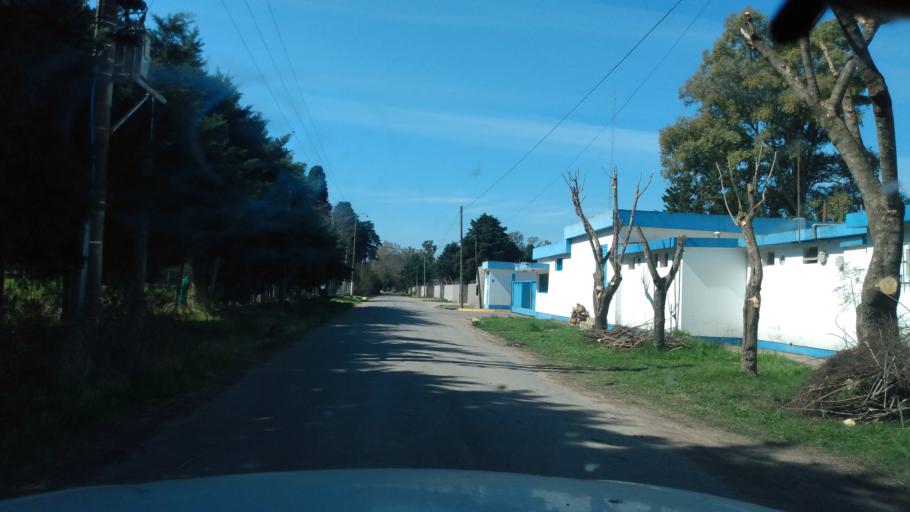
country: AR
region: Buenos Aires
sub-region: Partido de Lujan
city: Lujan
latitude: -34.5736
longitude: -59.1324
